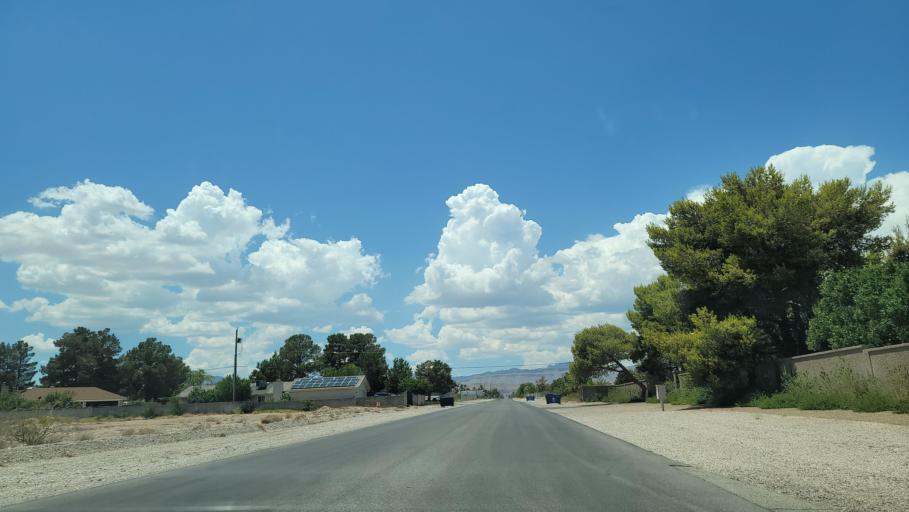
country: US
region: Nevada
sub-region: Clark County
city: Spring Valley
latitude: 36.0782
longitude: -115.2271
